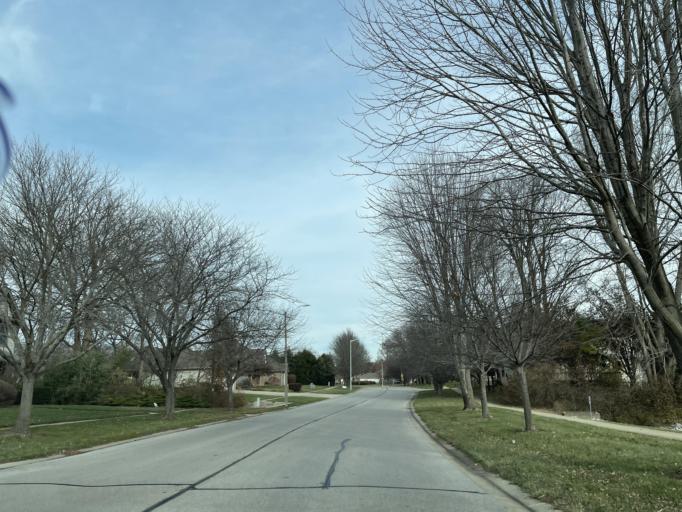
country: US
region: Illinois
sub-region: Sangamon County
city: Leland Grove
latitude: 39.7804
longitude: -89.7296
